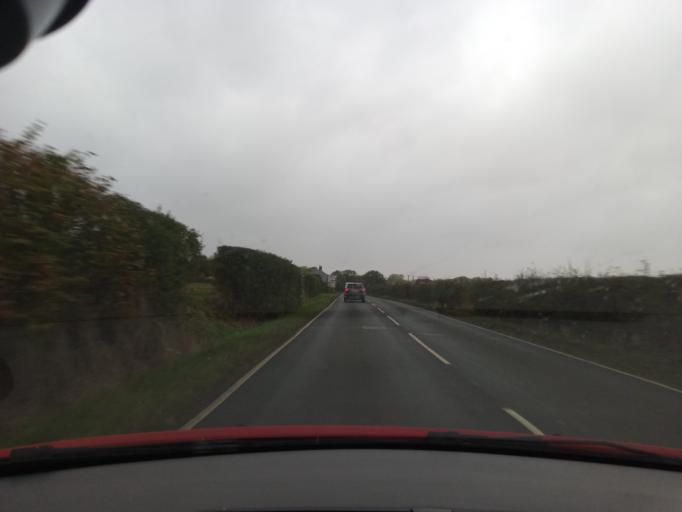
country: GB
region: England
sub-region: Suffolk
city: Kedington
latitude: 52.0556
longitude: 0.4959
